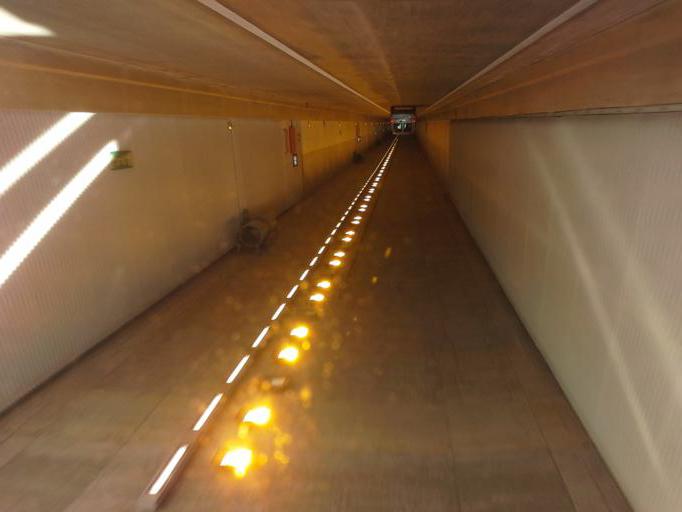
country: BE
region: Flanders
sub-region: Provincie Antwerpen
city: Kasterlee
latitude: 51.2296
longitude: 4.9613
